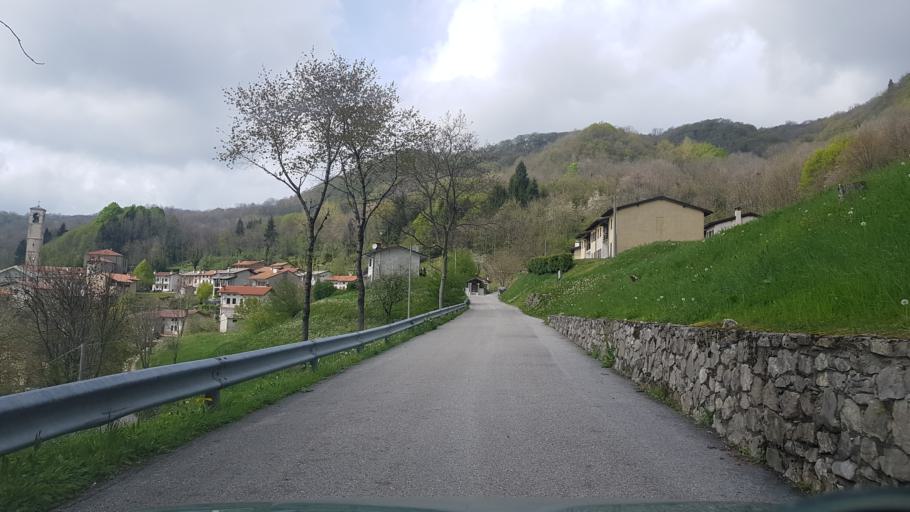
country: IT
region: Friuli Venezia Giulia
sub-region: Provincia di Udine
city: Attimis
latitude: 46.2050
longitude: 13.3474
